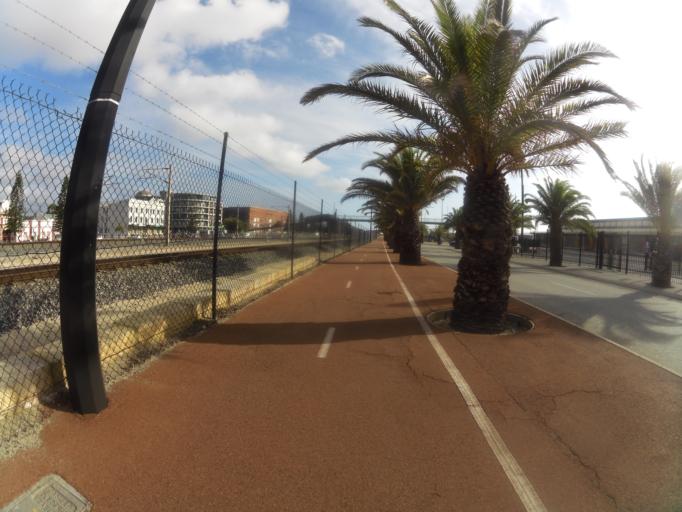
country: AU
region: Western Australia
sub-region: Fremantle
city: North Fremantle
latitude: -32.0479
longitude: 115.7488
